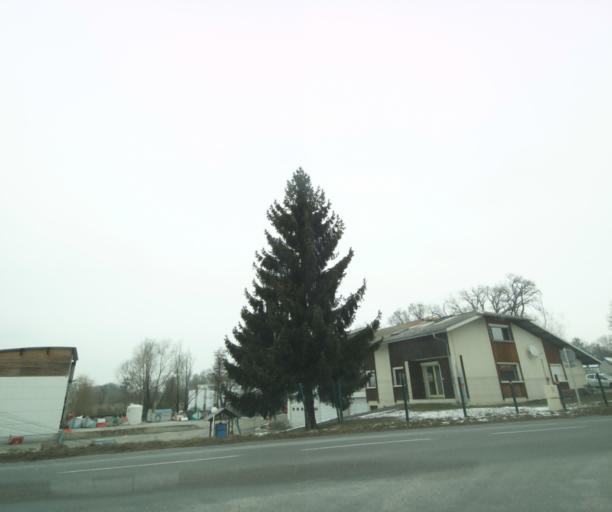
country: FR
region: Rhone-Alpes
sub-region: Departement de la Haute-Savoie
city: Reignier-Esery
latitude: 46.1340
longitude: 6.3007
